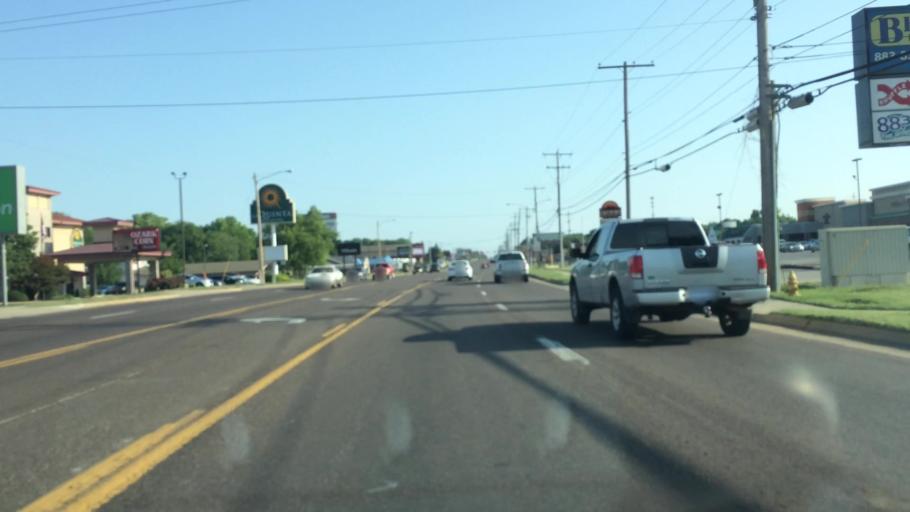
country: US
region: Missouri
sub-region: Greene County
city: Springfield
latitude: 37.1674
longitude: -93.2955
